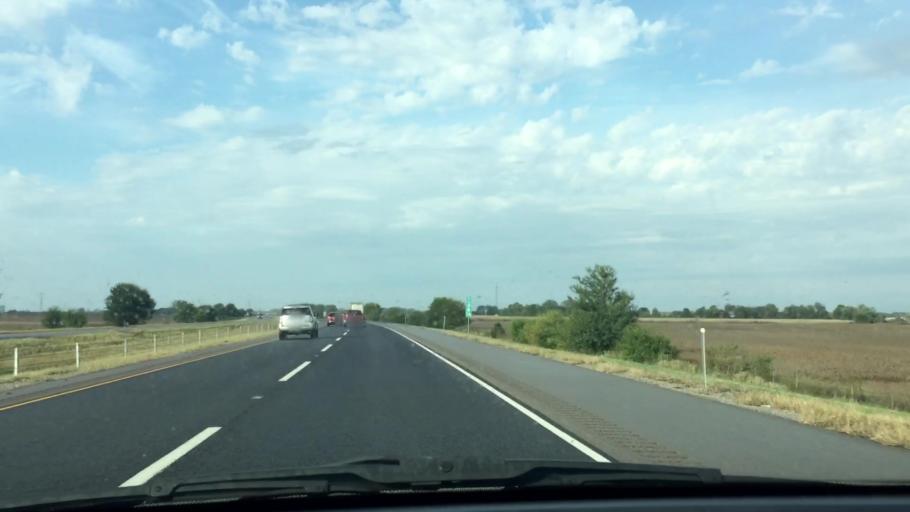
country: US
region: Illinois
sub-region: Lee County
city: Dixon
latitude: 41.7790
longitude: -89.5655
